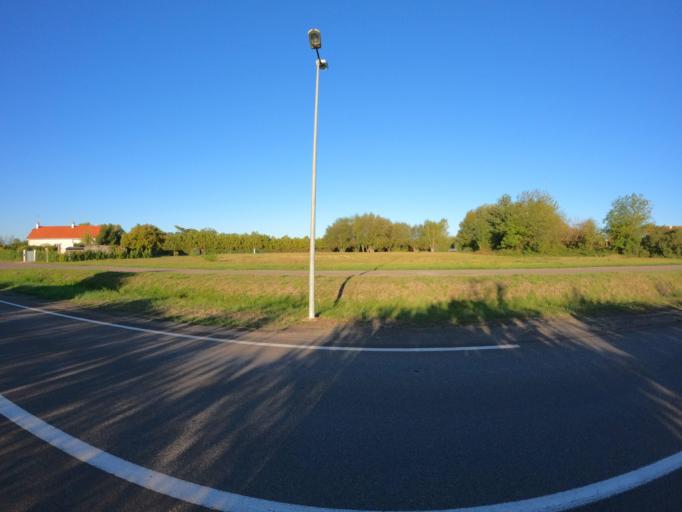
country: FR
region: Bourgogne
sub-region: Departement de Saone-et-Loire
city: Saint-Marcel
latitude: 46.7838
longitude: 4.9094
